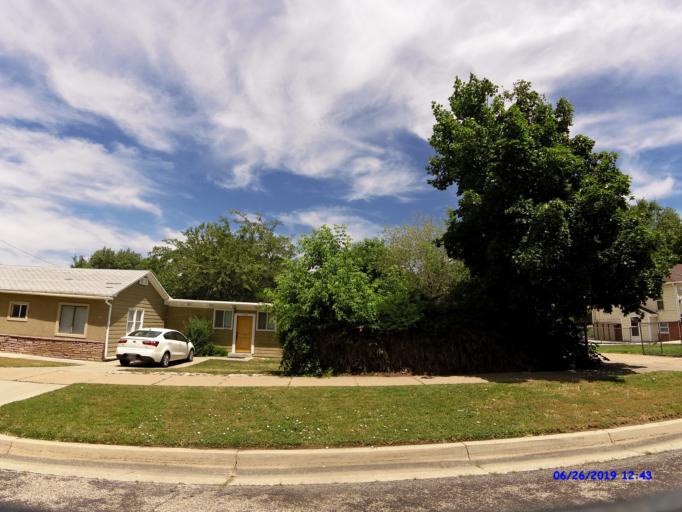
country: US
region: Utah
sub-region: Weber County
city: Ogden
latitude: 41.2278
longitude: -111.9494
